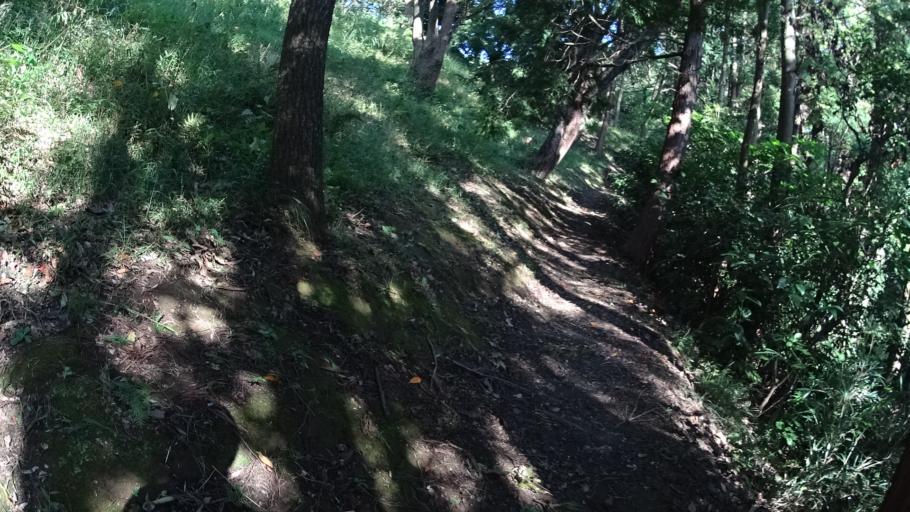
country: JP
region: Kanagawa
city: Zushi
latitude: 35.3560
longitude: 139.6004
